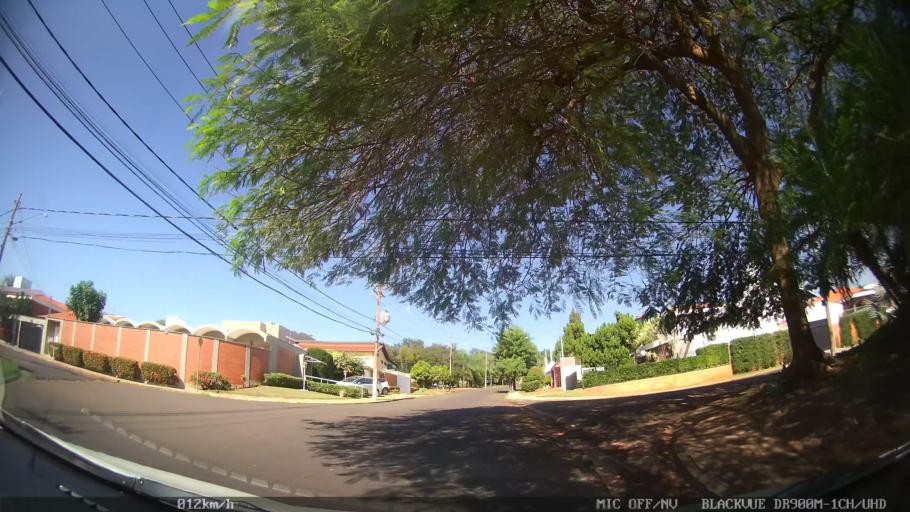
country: BR
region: Sao Paulo
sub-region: Ribeirao Preto
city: Ribeirao Preto
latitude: -21.1995
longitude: -47.7822
